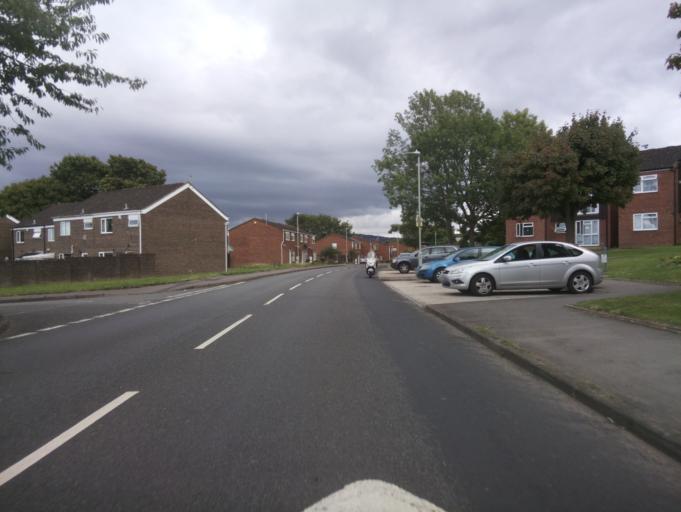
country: GB
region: England
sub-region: Gloucestershire
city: Gloucester
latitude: 51.8434
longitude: -2.2291
